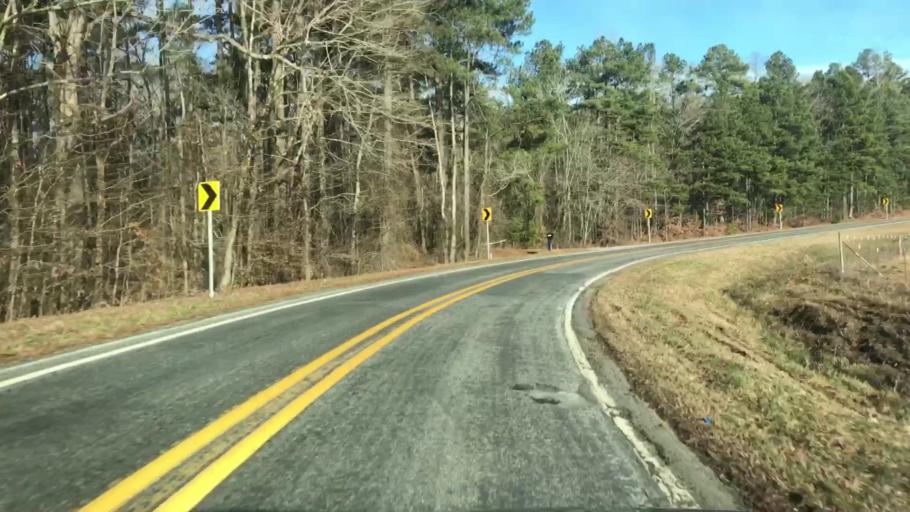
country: US
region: Arkansas
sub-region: Garland County
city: Rockwell
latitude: 34.4811
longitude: -93.2731
